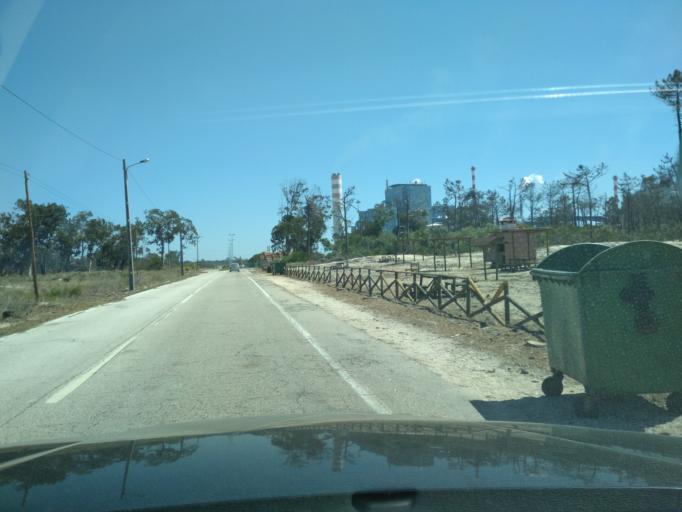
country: PT
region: Coimbra
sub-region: Figueira da Foz
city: Lavos
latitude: 40.0559
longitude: -8.8819
